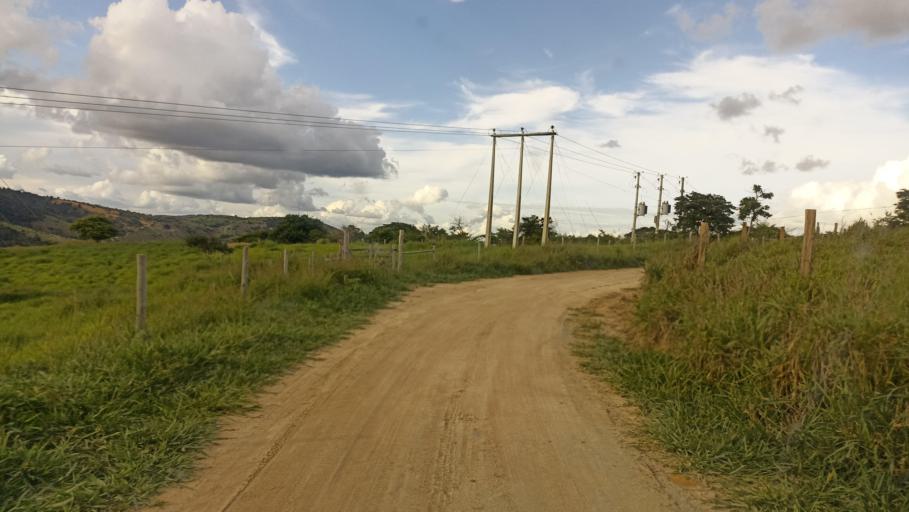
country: BR
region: Minas Gerais
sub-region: Almenara
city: Almenara
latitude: -16.5448
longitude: -40.4494
